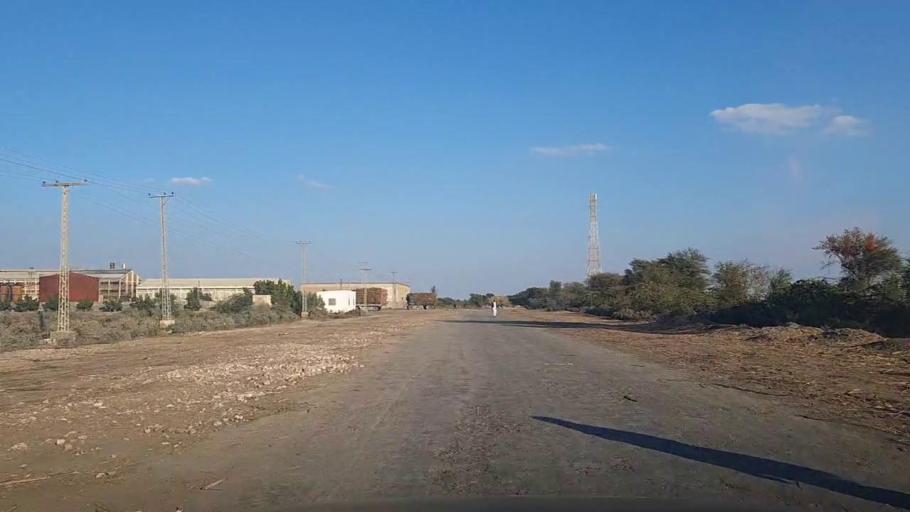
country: PK
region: Sindh
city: Jhol
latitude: 25.9272
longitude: 69.0040
